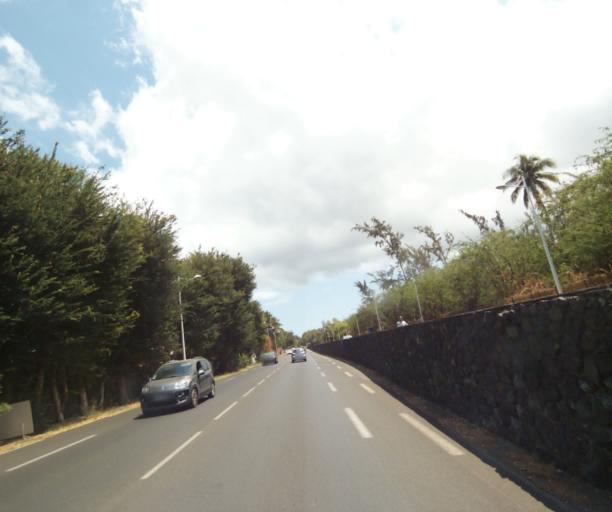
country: RE
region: Reunion
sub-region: Reunion
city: Trois-Bassins
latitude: -21.0791
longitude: 55.2290
